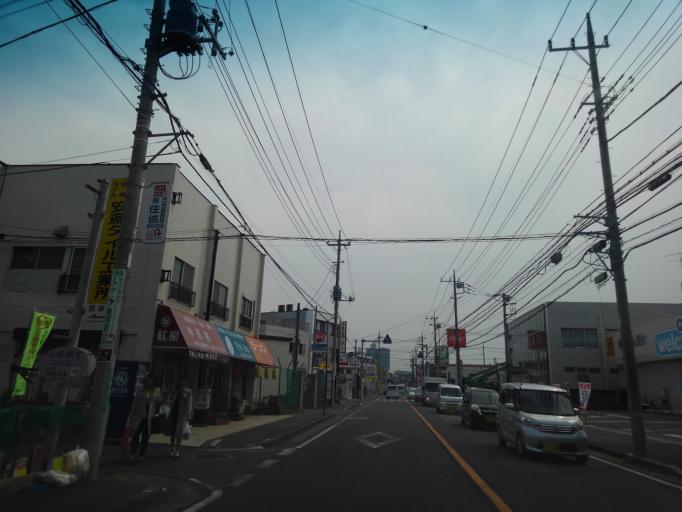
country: JP
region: Saitama
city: Tokorozawa
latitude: 35.8011
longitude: 139.4576
